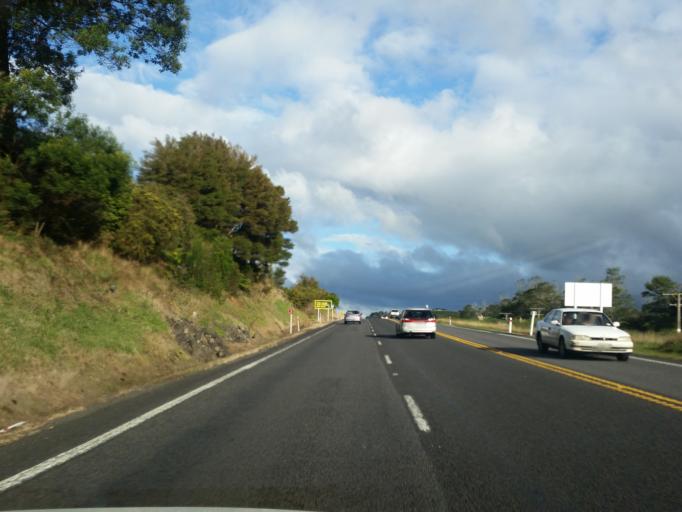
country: NZ
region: Bay of Plenty
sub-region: Western Bay of Plenty District
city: Katikati
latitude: -37.6425
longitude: 175.9641
